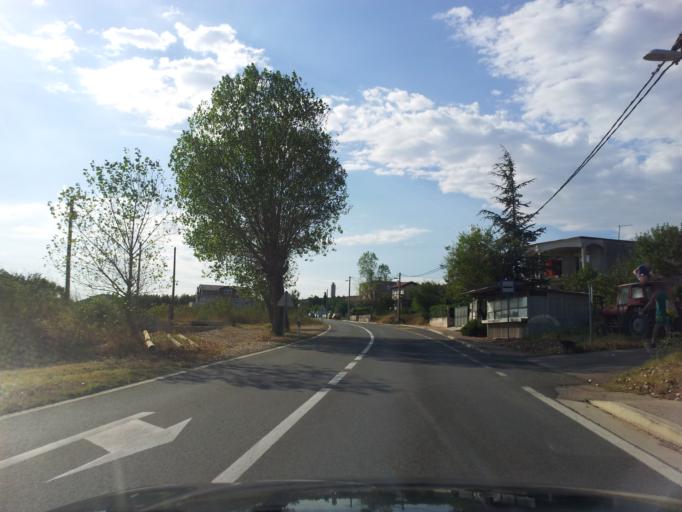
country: HR
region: Zadarska
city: Posedarje
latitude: 44.2163
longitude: 15.4670
